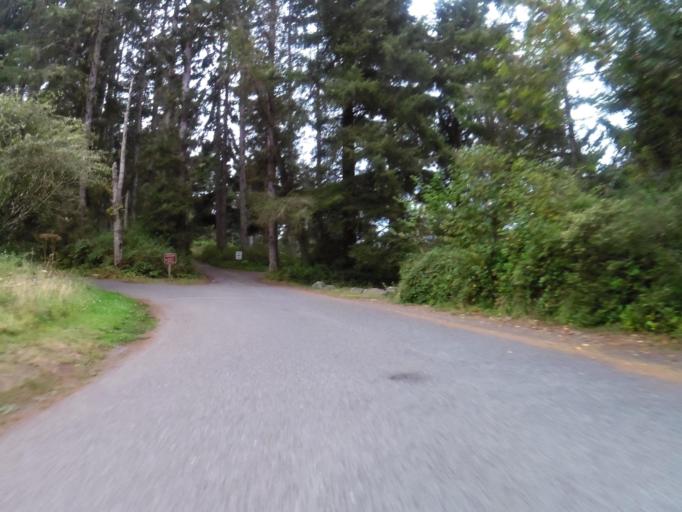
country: US
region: California
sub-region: Humboldt County
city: Westhaven-Moonstone
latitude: 41.1403
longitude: -124.1597
